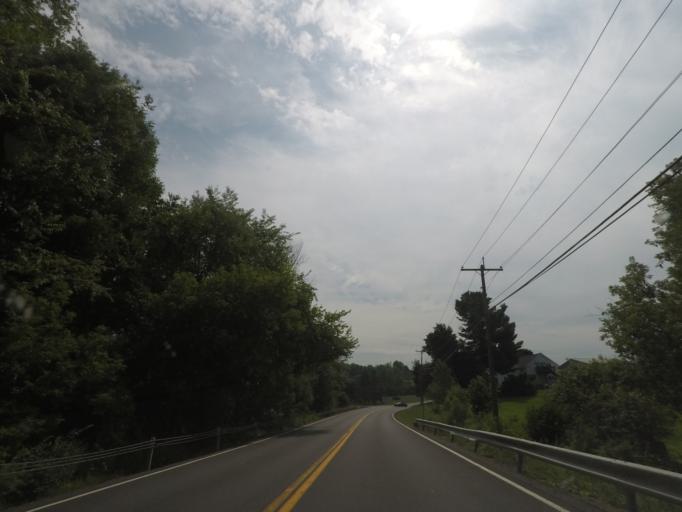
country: US
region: New York
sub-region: Saratoga County
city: Waterford
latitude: 42.7786
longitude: -73.6466
